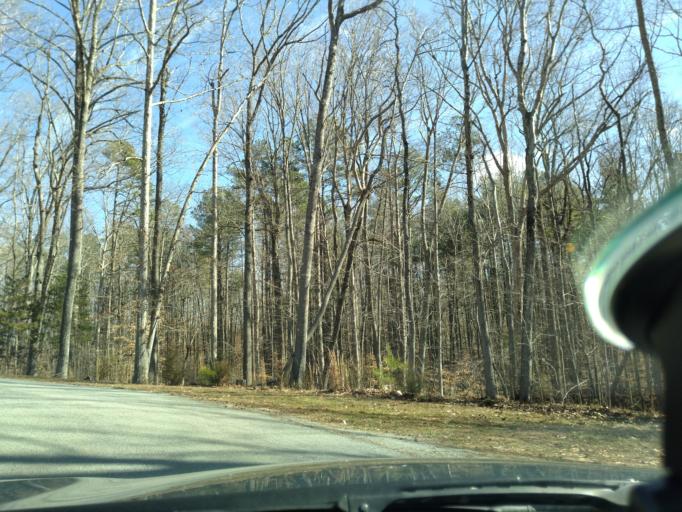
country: US
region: Virginia
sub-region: Nottoway County
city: Crewe
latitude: 37.1710
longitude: -78.2702
